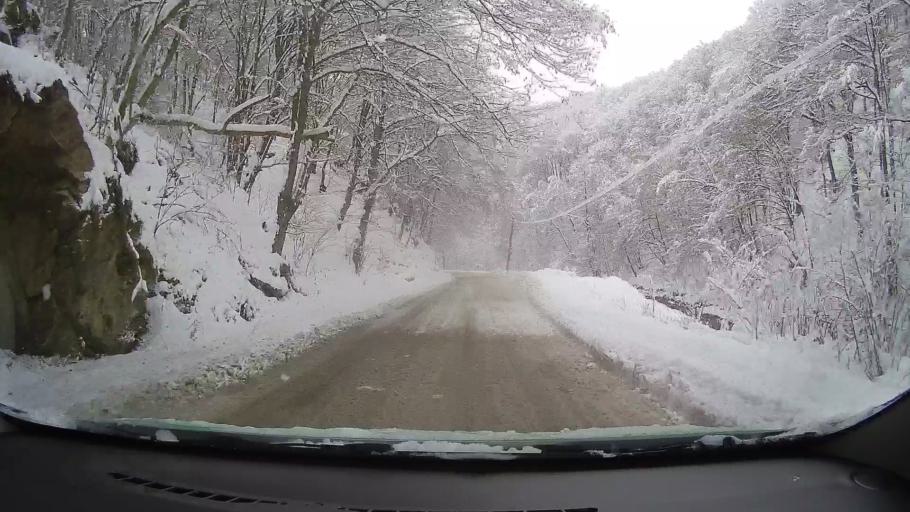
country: RO
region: Alba
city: Pianu de Sus
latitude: 45.8721
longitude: 23.4927
